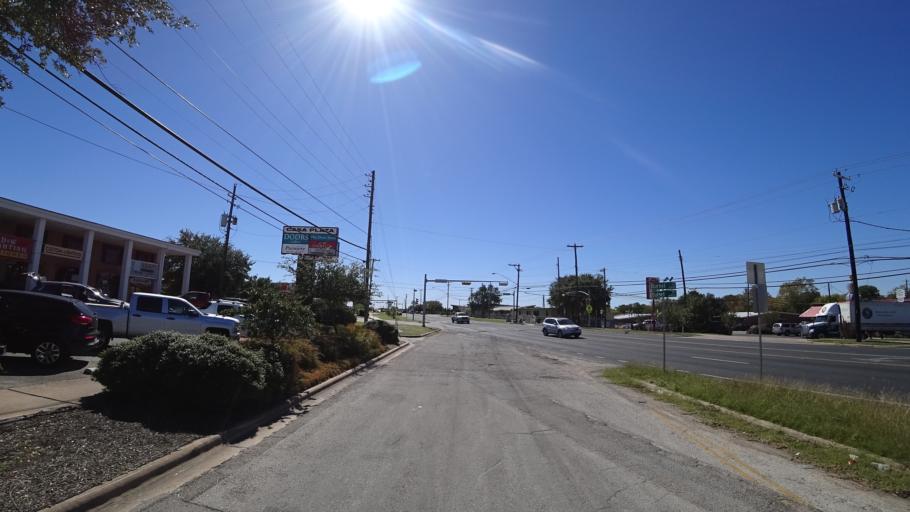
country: US
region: Texas
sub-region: Travis County
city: Austin
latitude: 30.3390
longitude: -97.7390
